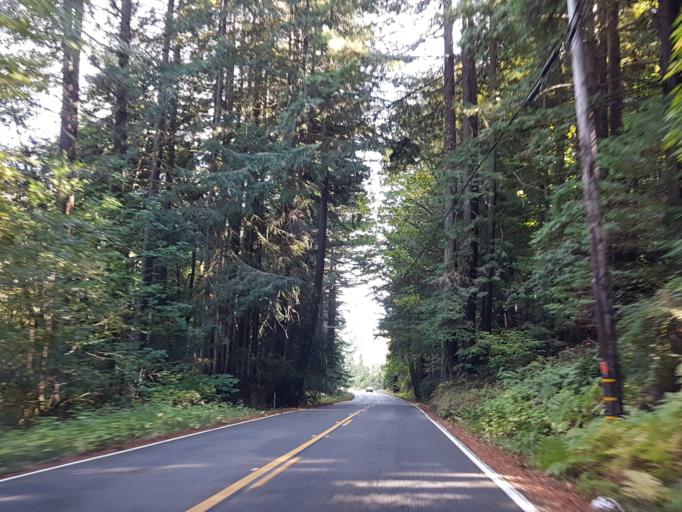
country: US
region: California
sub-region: Humboldt County
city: Rio Dell
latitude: 40.4143
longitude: -123.9611
